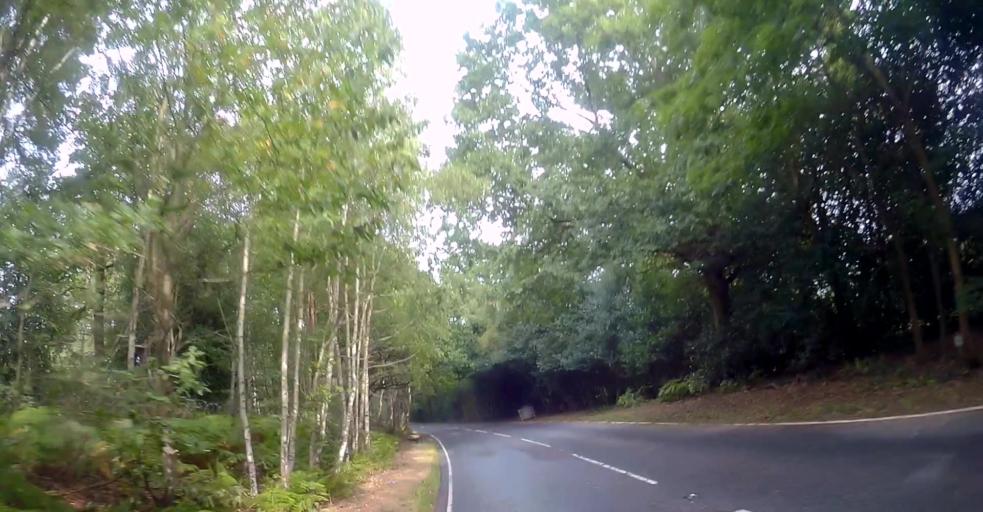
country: GB
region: England
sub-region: Surrey
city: Pirbright
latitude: 51.3004
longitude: -0.6627
